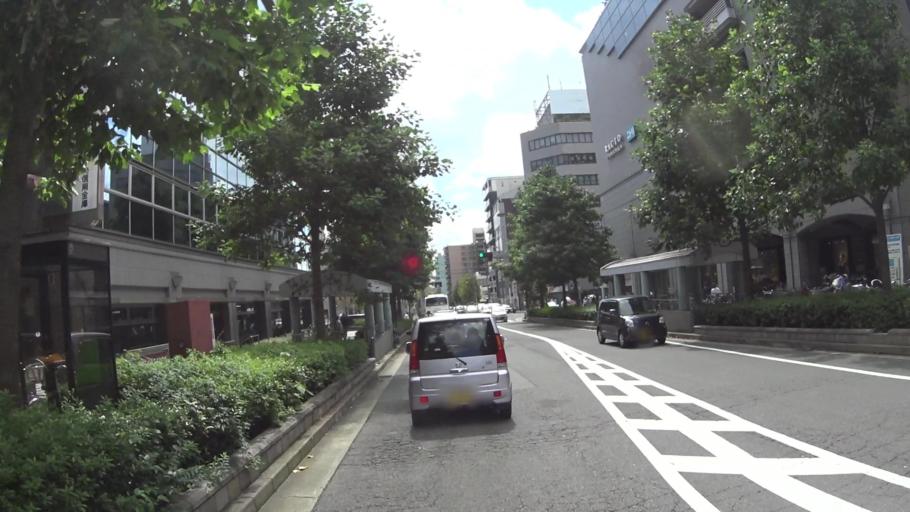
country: JP
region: Shiga Prefecture
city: Otsu-shi
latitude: 34.9904
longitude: 135.8173
